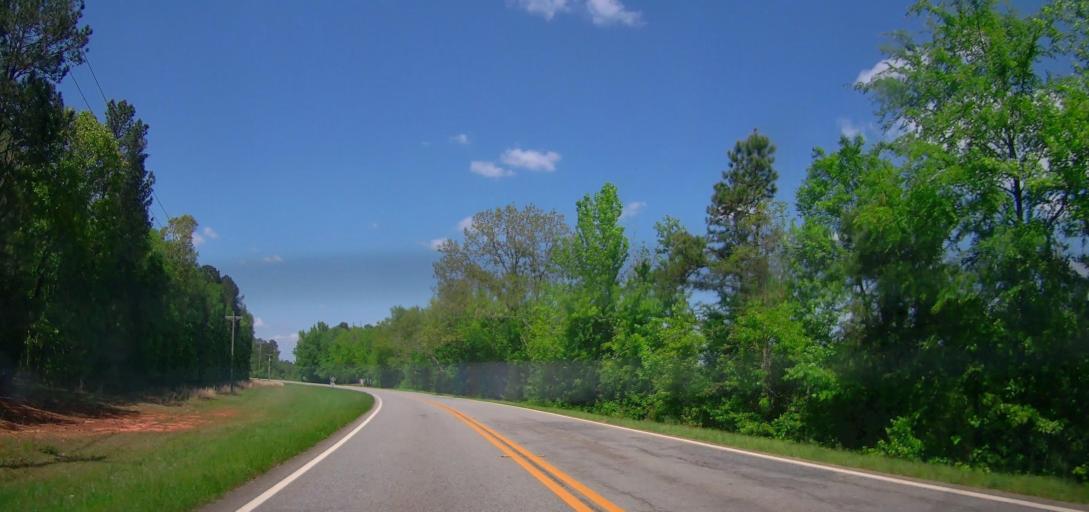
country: US
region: Georgia
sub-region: Putnam County
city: Eatonton
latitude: 33.3056
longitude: -83.3018
